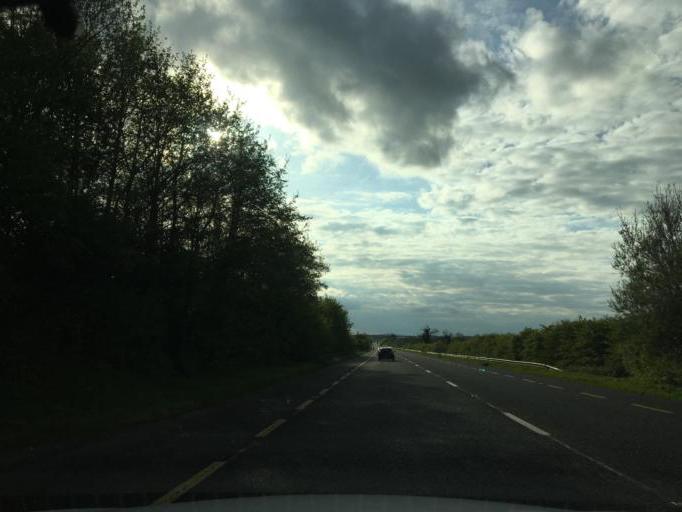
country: IE
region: Leinster
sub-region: Loch Garman
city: Loch Garman
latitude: 52.3461
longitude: -6.6016
